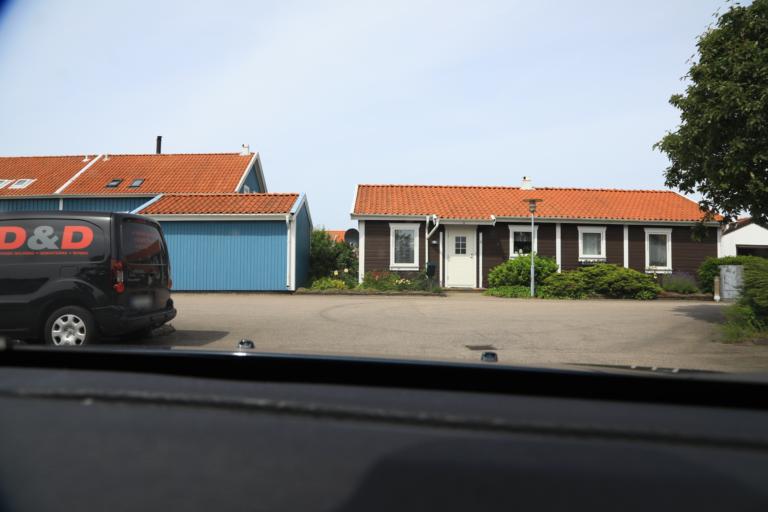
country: SE
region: Halland
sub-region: Varbergs Kommun
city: Traslovslage
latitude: 57.1037
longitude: 12.2967
